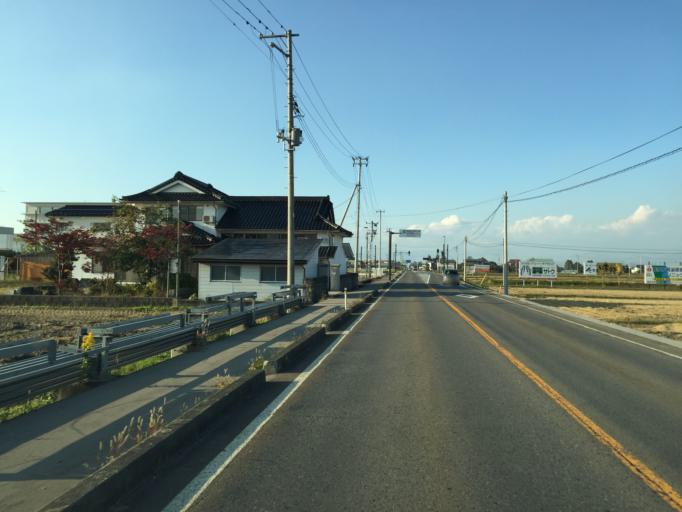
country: JP
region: Fukushima
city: Kitakata
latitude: 37.5502
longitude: 139.9101
